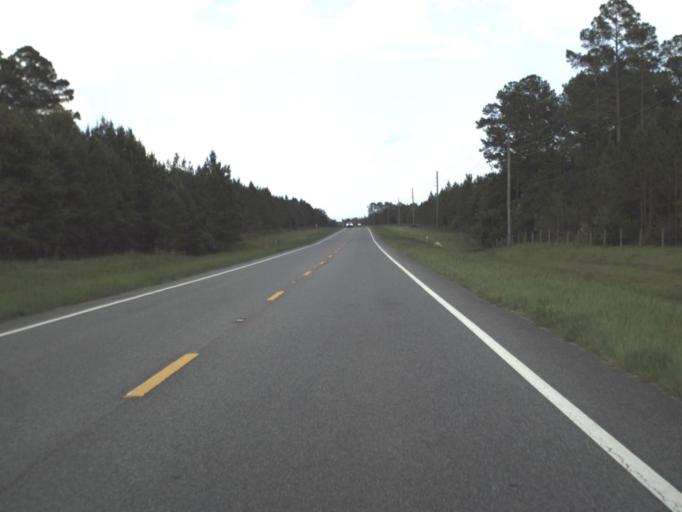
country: US
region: Florida
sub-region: Clay County
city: Middleburg
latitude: 29.9781
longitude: -81.8823
